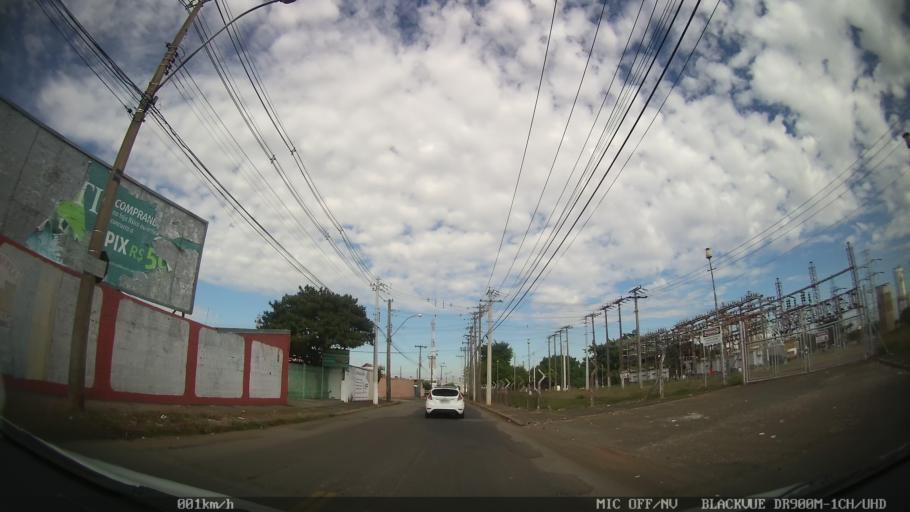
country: BR
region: Sao Paulo
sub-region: Americana
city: Americana
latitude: -22.7405
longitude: -47.3546
